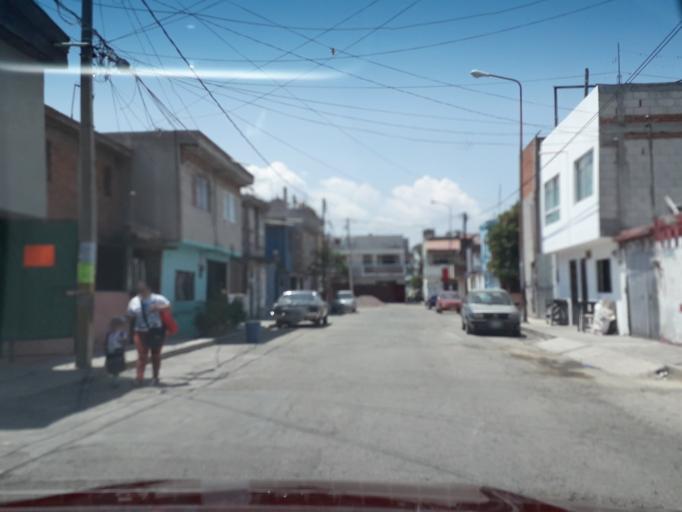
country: MX
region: Puebla
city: Tlazcalancingo
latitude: 18.9991
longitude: -98.2377
